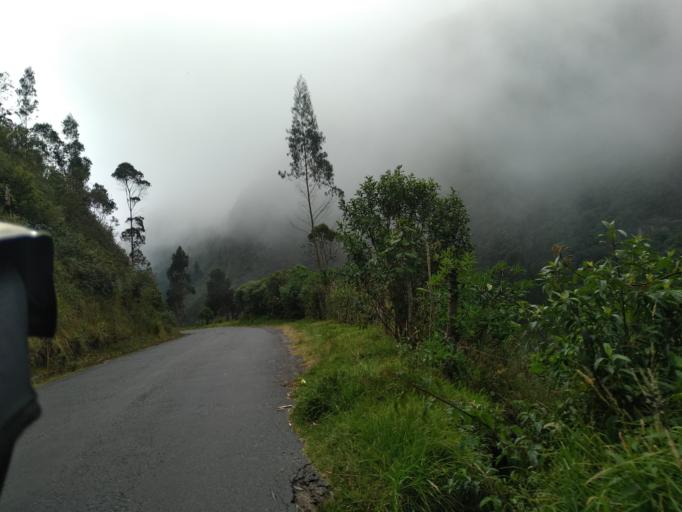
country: EC
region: Cotopaxi
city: Saquisili
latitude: -0.7007
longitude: -78.8017
